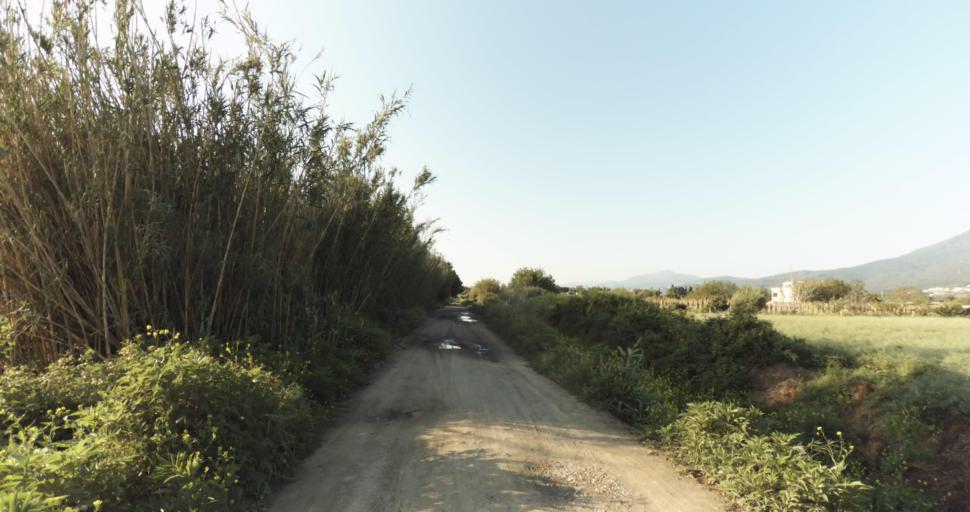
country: FR
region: Corsica
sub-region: Departement de la Haute-Corse
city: Biguglia
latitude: 42.6140
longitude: 9.4461
